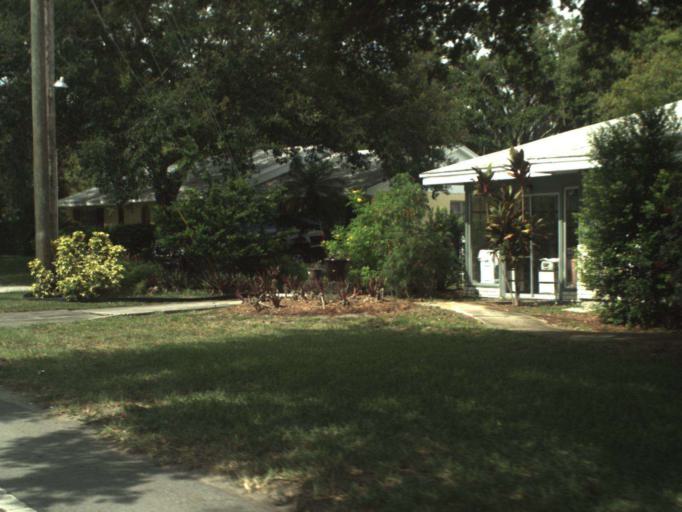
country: US
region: Florida
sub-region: Indian River County
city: Vero Beach South
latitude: 27.6407
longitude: -80.4303
